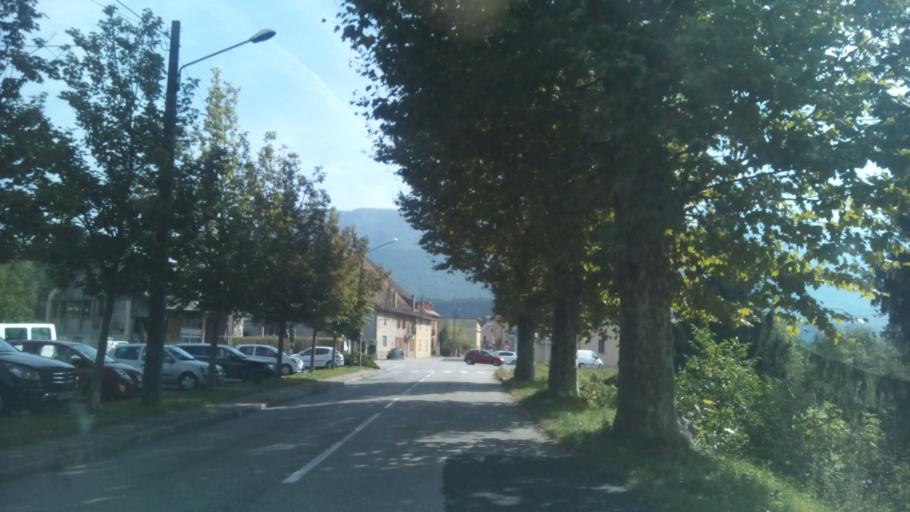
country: FR
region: Rhone-Alpes
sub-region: Departement de la Savoie
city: Les Echelles
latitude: 45.4390
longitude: 5.7504
